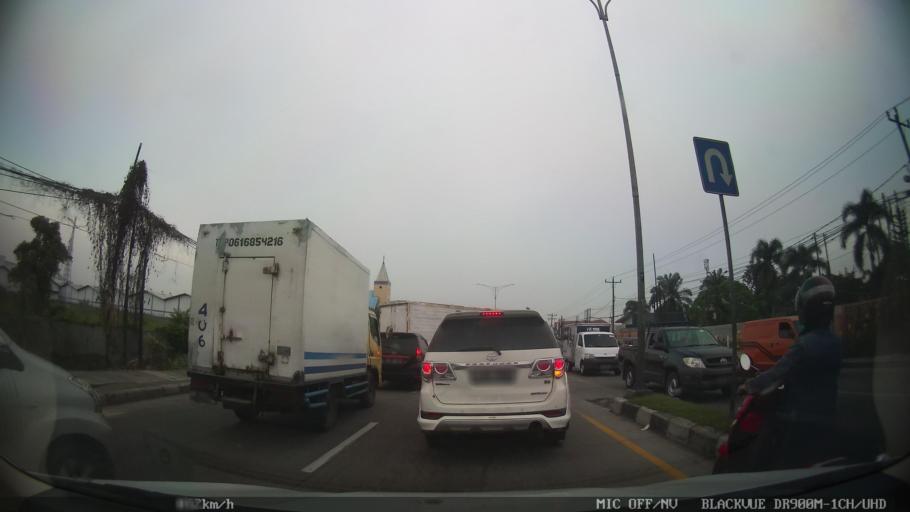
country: ID
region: North Sumatra
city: Deli Tua
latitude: 3.5324
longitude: 98.7338
